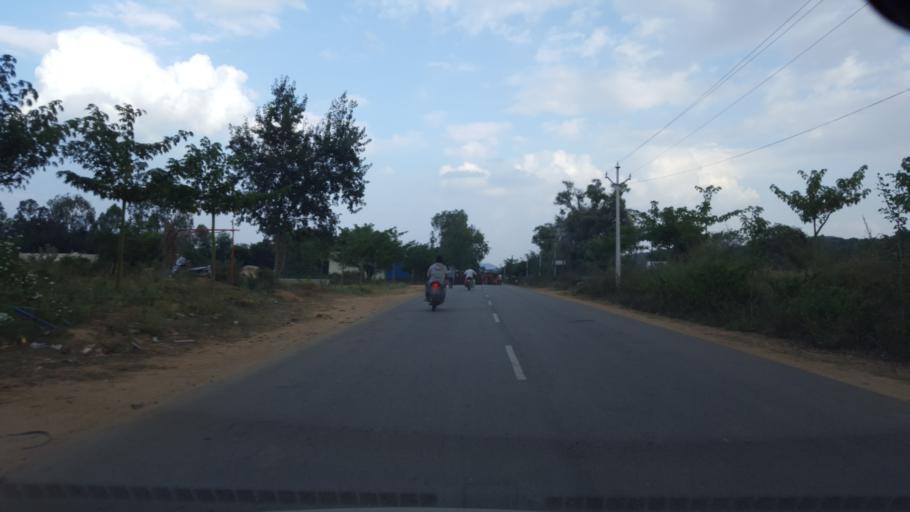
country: IN
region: Telangana
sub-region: Mahbubnagar
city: Mahbubnagar
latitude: 16.7598
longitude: 77.9586
